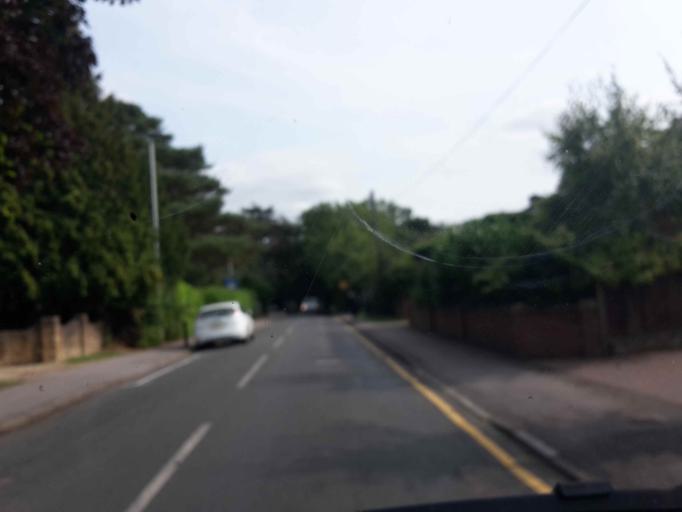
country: GB
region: England
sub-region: Wokingham
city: Wokingham
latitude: 51.4082
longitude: -0.8258
